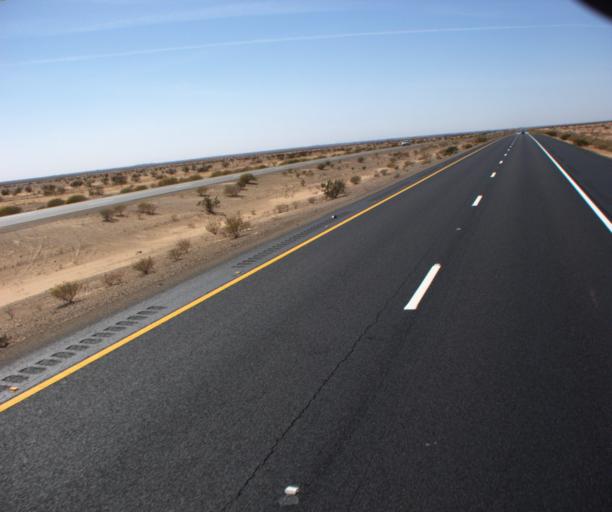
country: US
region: Arizona
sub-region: Yuma County
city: Somerton
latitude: 32.4953
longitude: -114.5791
